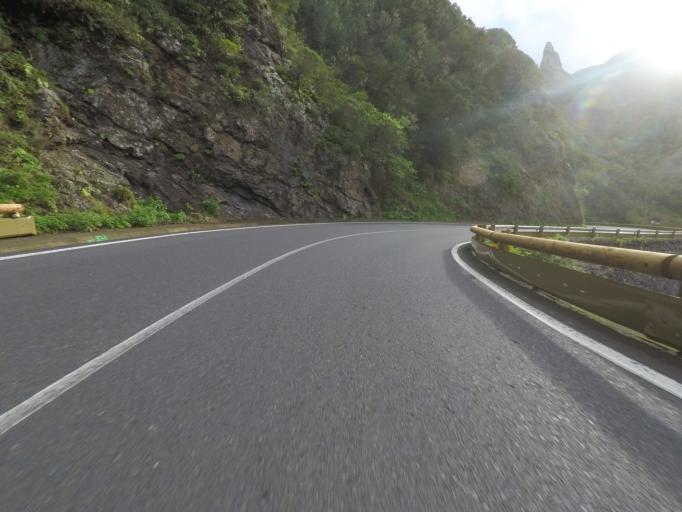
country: ES
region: Canary Islands
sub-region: Provincia de Santa Cruz de Tenerife
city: Hermigua
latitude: 28.1353
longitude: -17.1995
